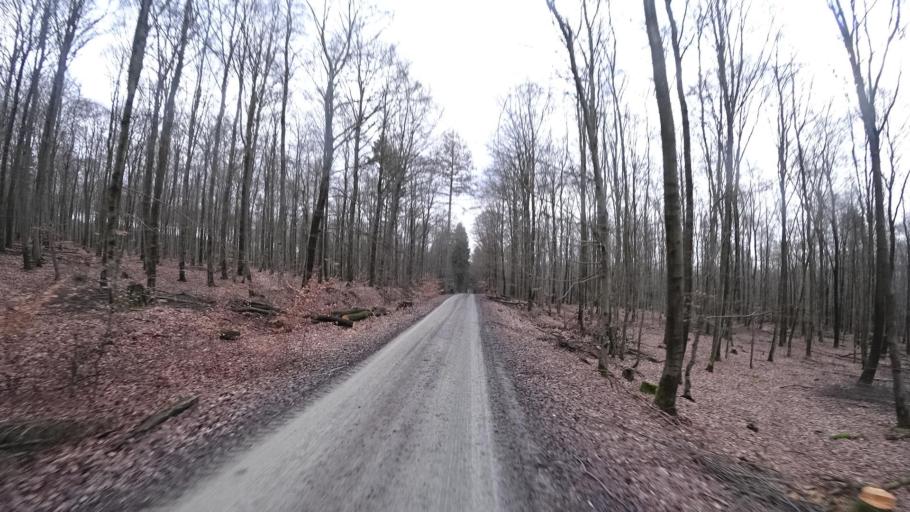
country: DE
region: Rheinland-Pfalz
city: Arzbach
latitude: 50.4140
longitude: 7.7633
